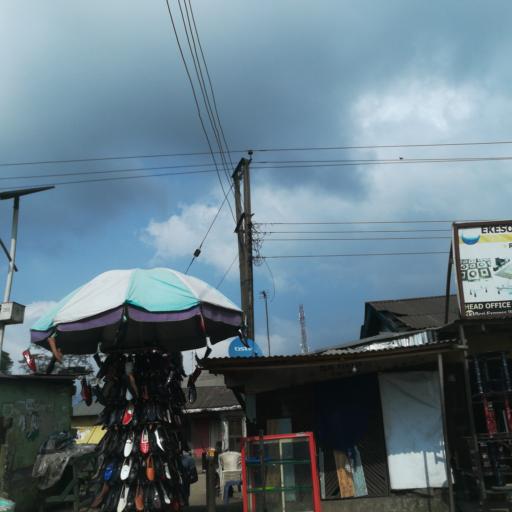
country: NG
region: Rivers
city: Okrika
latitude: 4.7853
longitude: 7.1173
